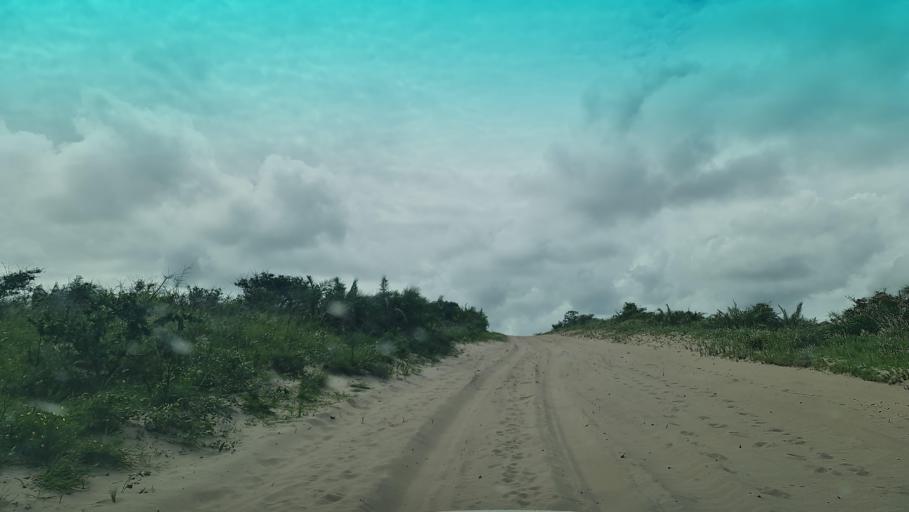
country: MZ
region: Maputo
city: Manhica
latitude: -25.4474
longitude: 32.9514
